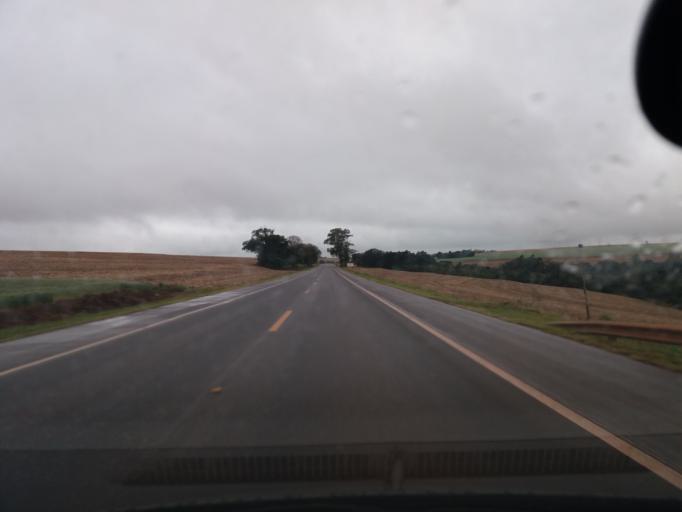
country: BR
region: Parana
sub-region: Campo Mourao
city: Campo Mourao
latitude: -24.3293
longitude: -52.6547
